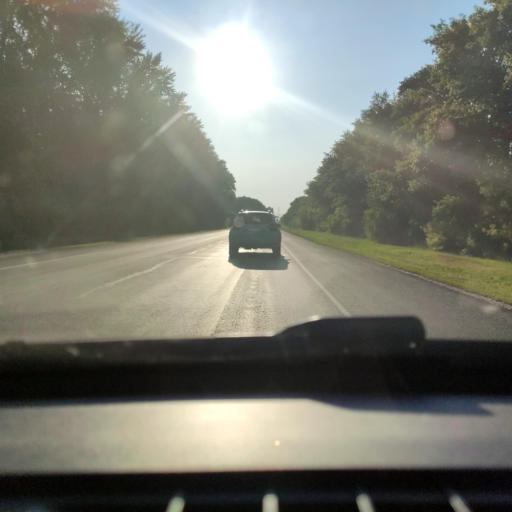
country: RU
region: Voronezj
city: Kashirskoye
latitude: 51.4932
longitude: 39.6074
